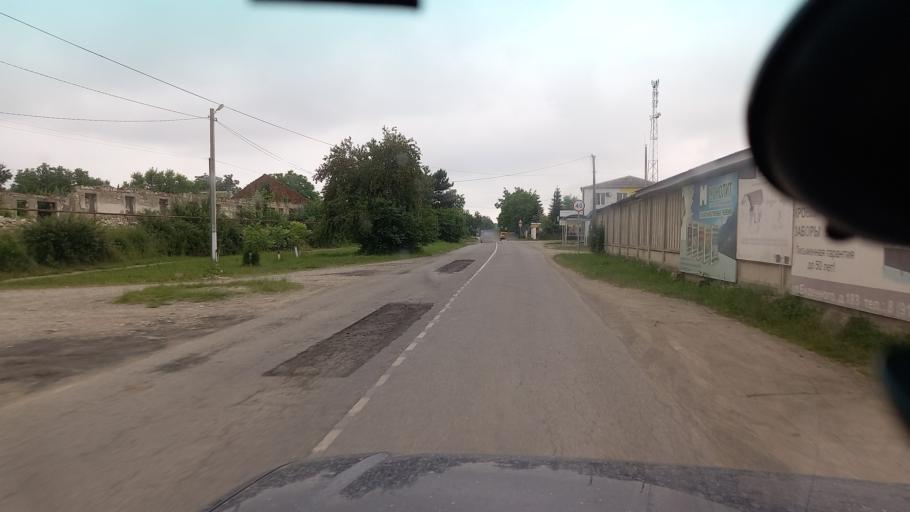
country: RU
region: Krasnodarskiy
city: Mostovskoy
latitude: 44.4182
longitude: 40.7779
